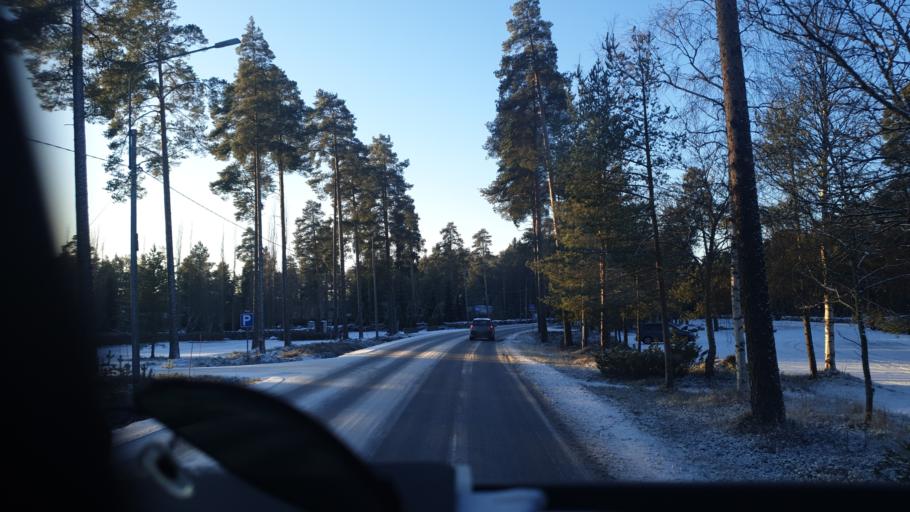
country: FI
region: Central Ostrobothnia
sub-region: Kokkola
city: Kokkola
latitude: 63.8277
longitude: 23.0999
